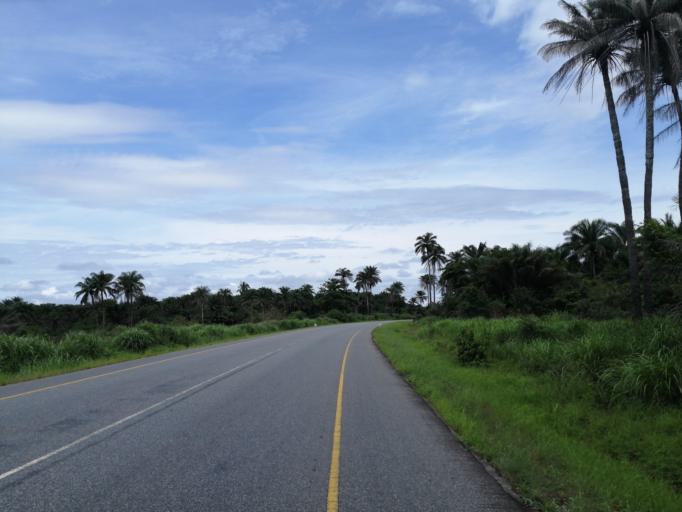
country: SL
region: Northern Province
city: Port Loko
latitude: 8.7490
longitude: -12.9193
